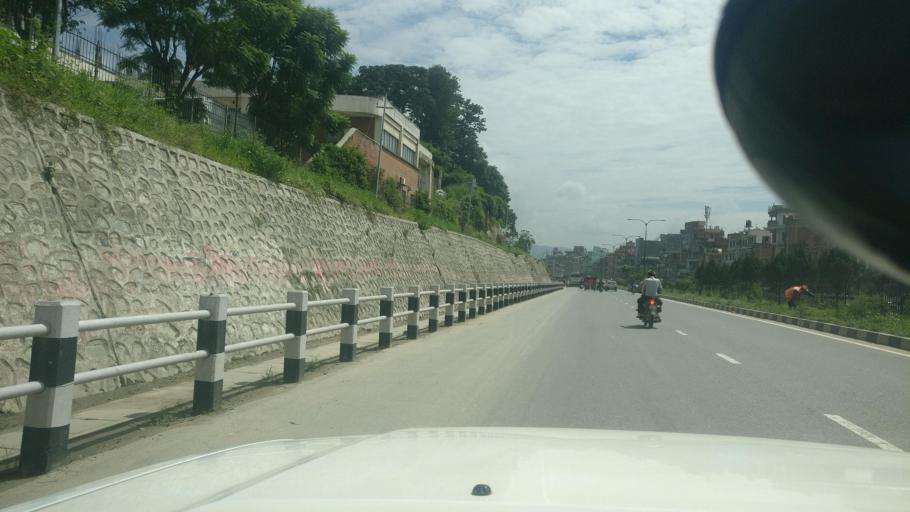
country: NP
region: Central Region
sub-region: Bagmati Zone
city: Bhaktapur
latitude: 27.6734
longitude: 85.3830
